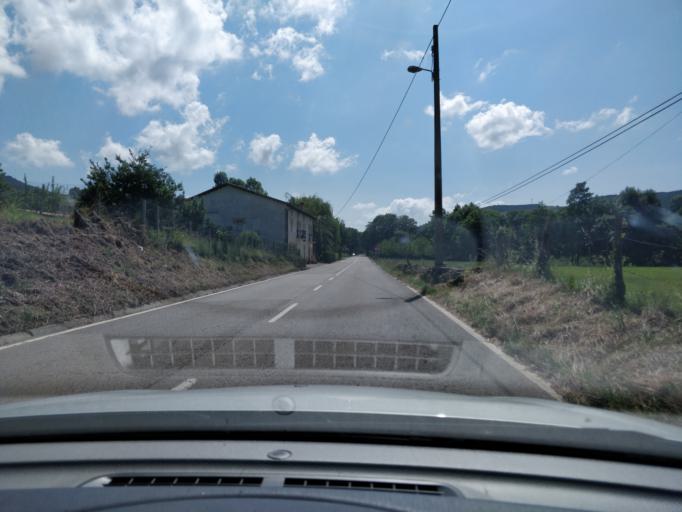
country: ES
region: Cantabria
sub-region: Provincia de Cantabria
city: Corvera
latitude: 43.2691
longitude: -3.9245
